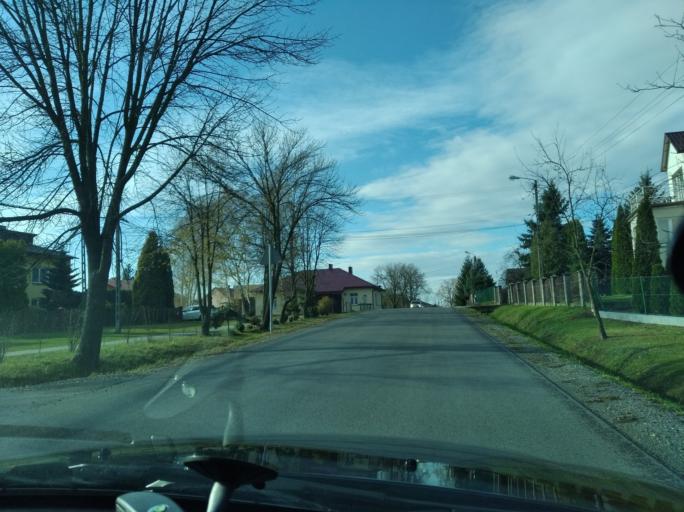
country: PL
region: Subcarpathian Voivodeship
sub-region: Powiat ropczycko-sedziszowski
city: Sedziszow Malopolski
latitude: 50.0791
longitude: 21.7367
